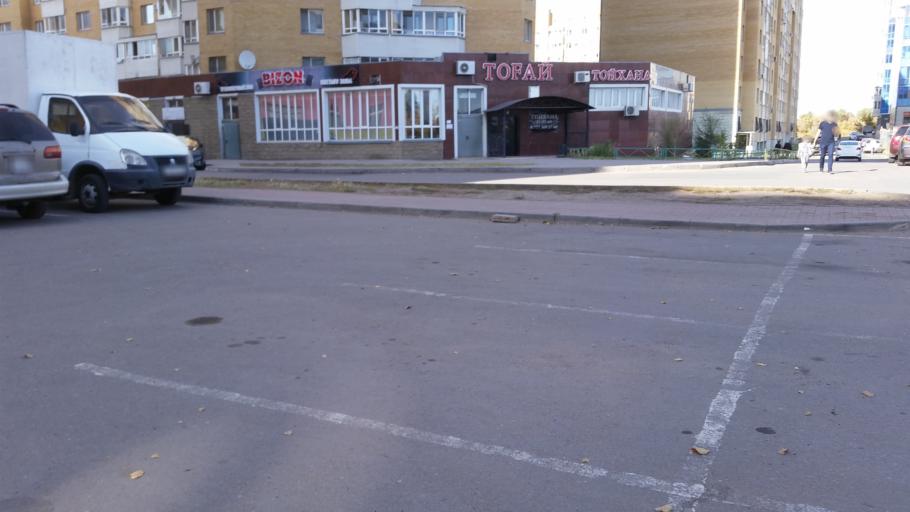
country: KZ
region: Astana Qalasy
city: Astana
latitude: 51.1560
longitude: 71.5094
